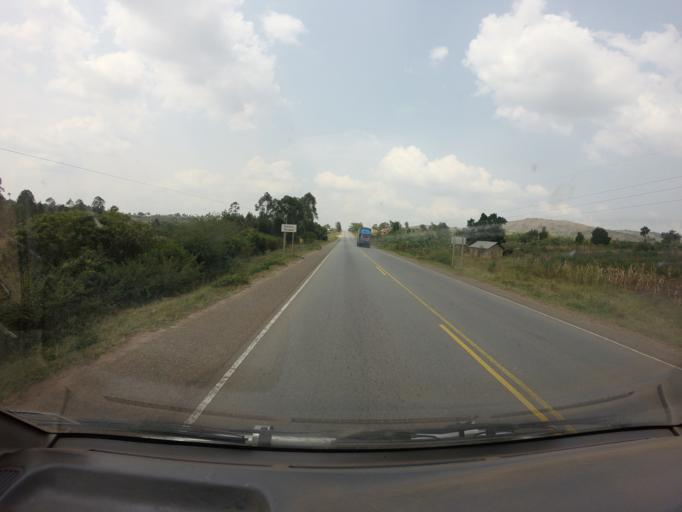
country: UG
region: Central Region
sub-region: Lyantonde District
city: Lyantonde
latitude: -0.3835
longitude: 31.2267
